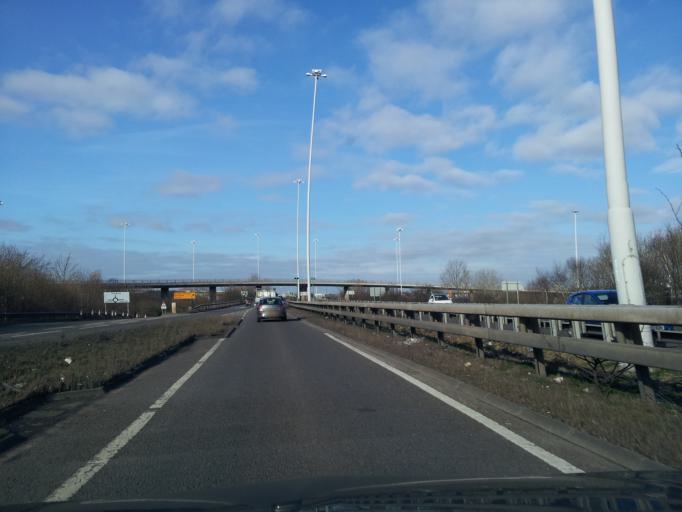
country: GB
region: England
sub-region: Nottingham
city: Nottingham
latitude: 52.9275
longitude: -1.1679
